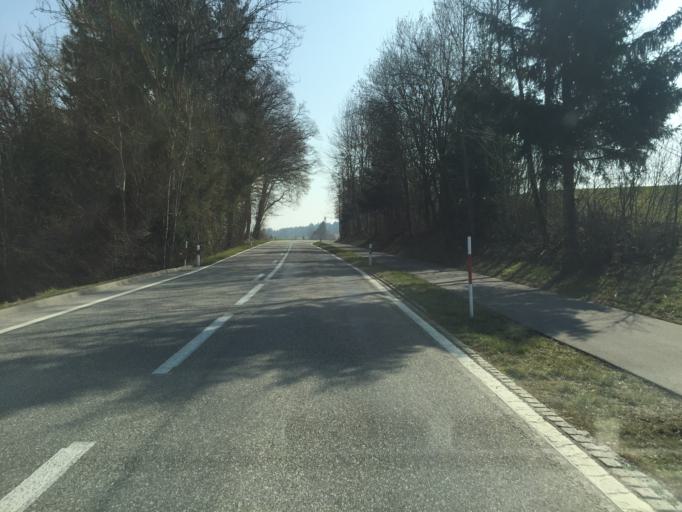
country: CH
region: Thurgau
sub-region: Frauenfeld District
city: Huttwilen
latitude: 47.5983
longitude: 8.8857
